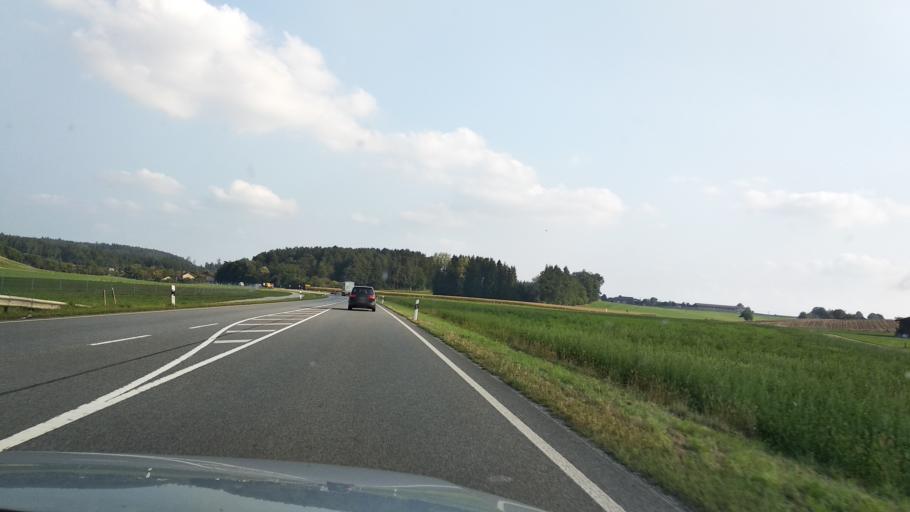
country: DE
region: Bavaria
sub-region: Upper Bavaria
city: Babensham
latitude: 48.0522
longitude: 12.2803
